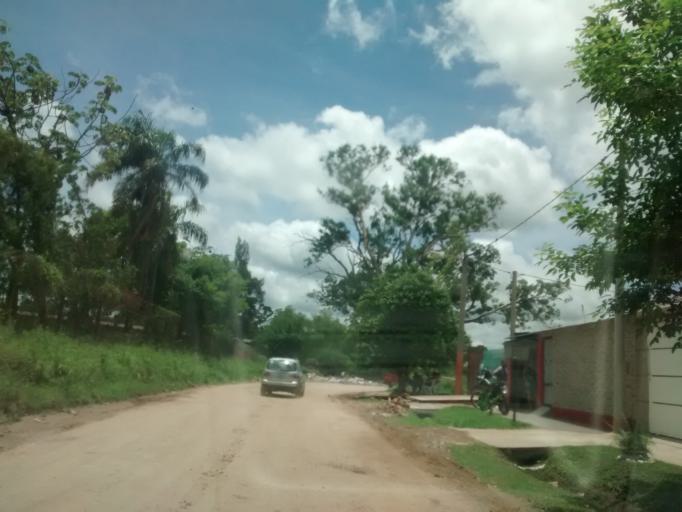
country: AR
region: Chaco
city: Fontana
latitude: -27.4269
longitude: -59.0078
